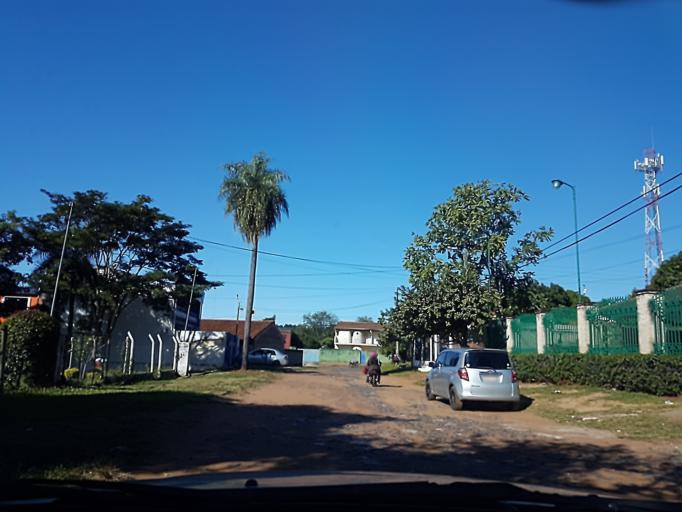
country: PY
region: Central
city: Nemby
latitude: -25.3960
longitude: -57.5429
